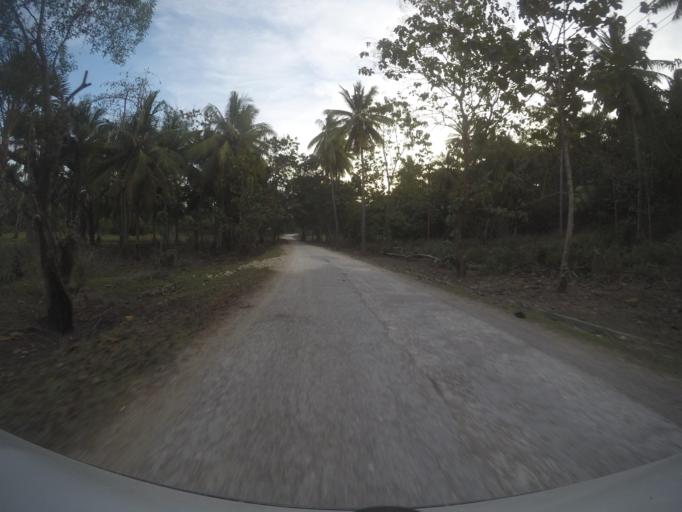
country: TL
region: Viqueque
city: Viqueque
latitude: -8.9419
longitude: 126.4363
